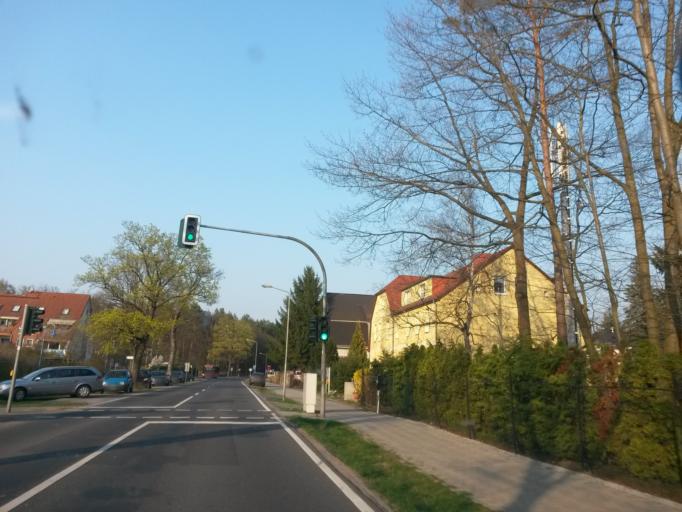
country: DE
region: Brandenburg
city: Grunheide
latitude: 52.4345
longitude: 13.8352
